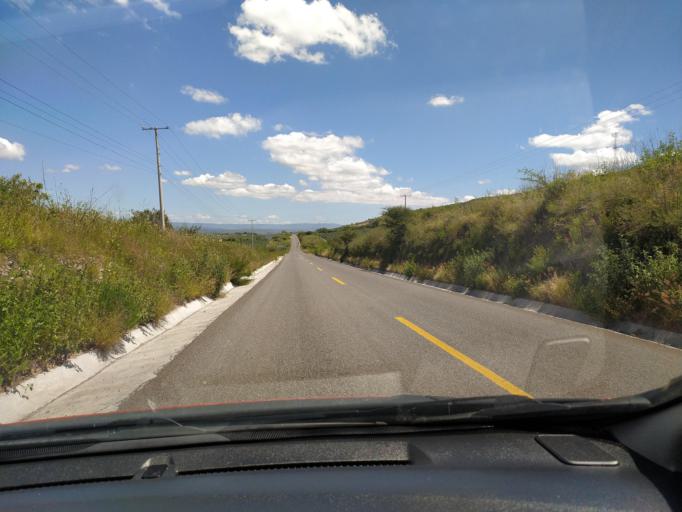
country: MX
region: Guanajuato
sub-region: Purisima del Rincon
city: Monte Grande
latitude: 21.0304
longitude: -101.9242
